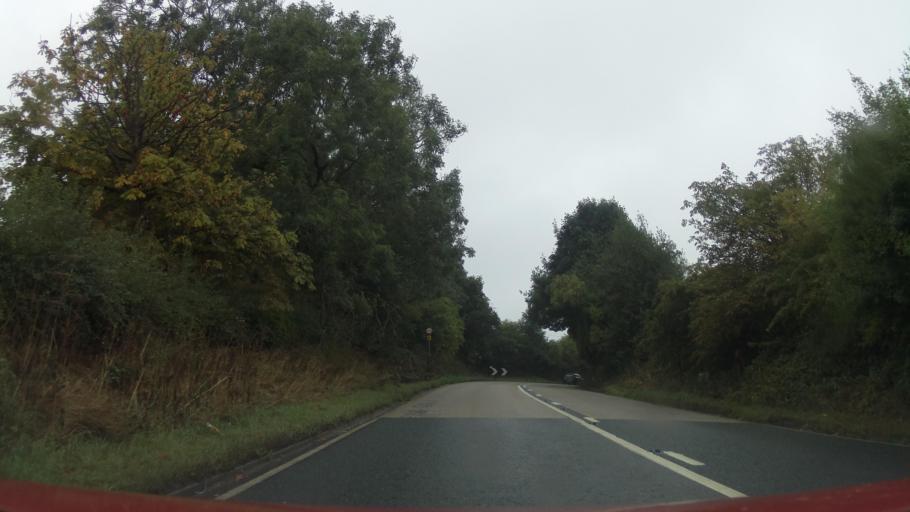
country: GB
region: England
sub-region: North Yorkshire
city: Pannal
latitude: 53.9531
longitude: -1.5349
